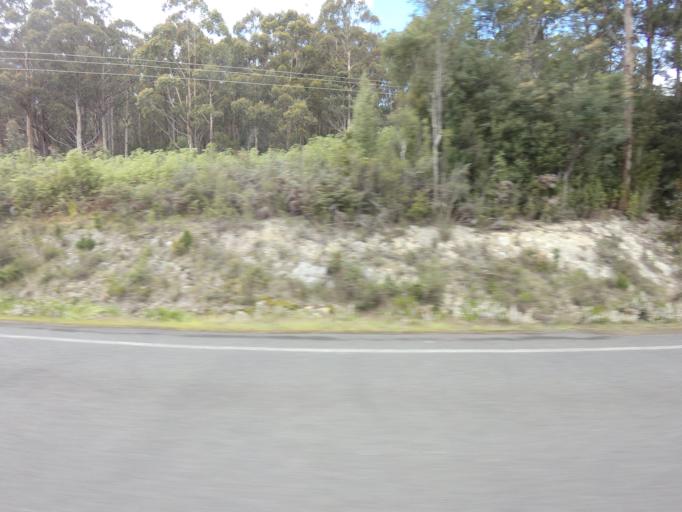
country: AU
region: Tasmania
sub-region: Huon Valley
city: Cygnet
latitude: -43.2751
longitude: 147.0093
